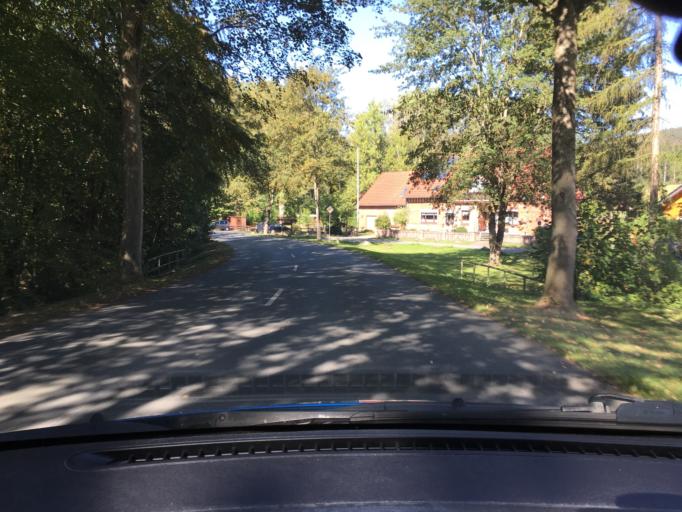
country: DE
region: Lower Saxony
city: Barsinghausen
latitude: 52.2595
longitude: 9.4416
